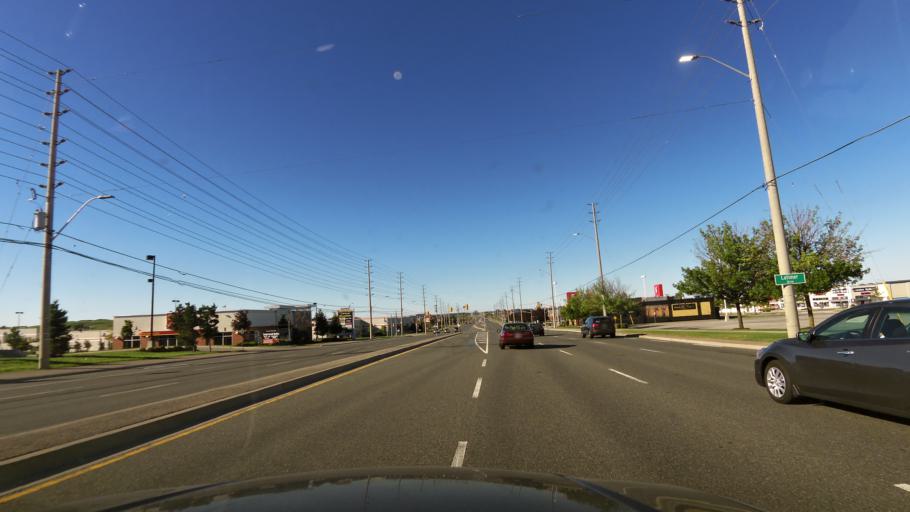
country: CA
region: Ontario
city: Mississauga
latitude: 43.6102
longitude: -79.6979
